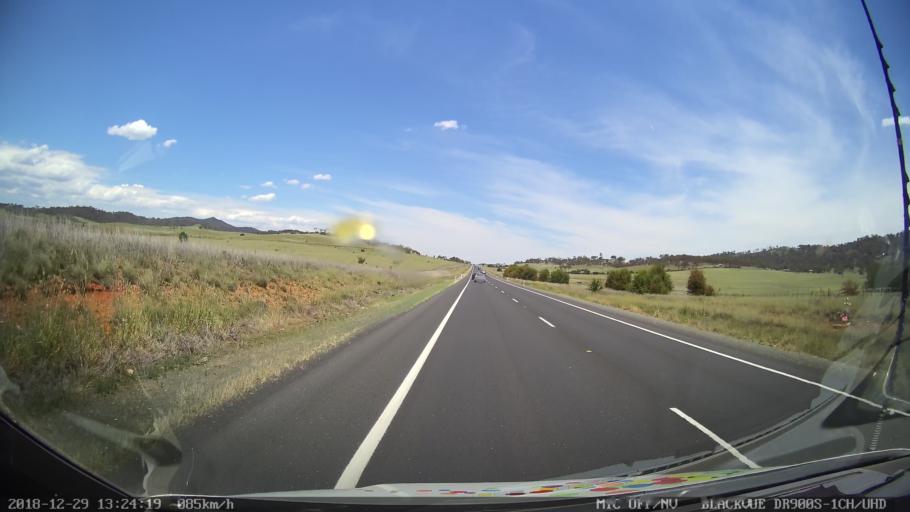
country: AU
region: New South Wales
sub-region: Cooma-Monaro
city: Cooma
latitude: -35.8279
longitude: 149.1626
